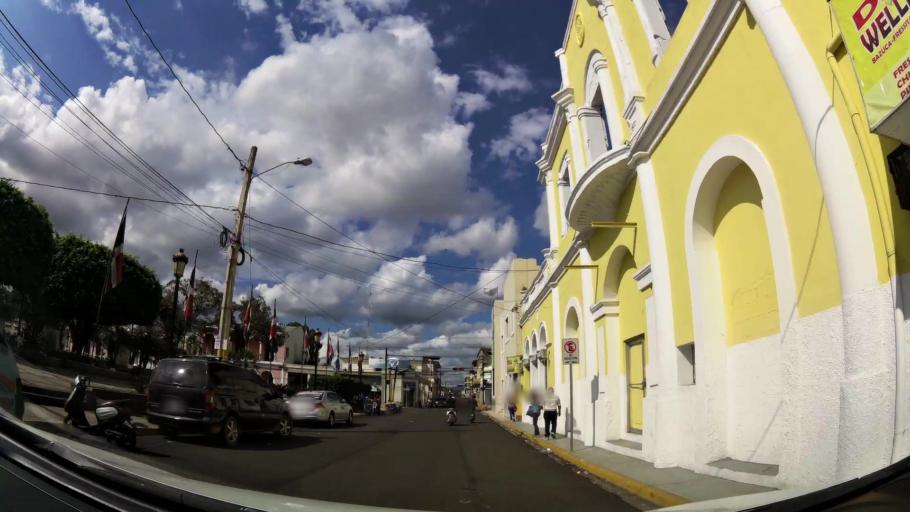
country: DO
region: La Vega
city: Concepcion de La Vega
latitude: 19.2245
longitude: -70.5323
